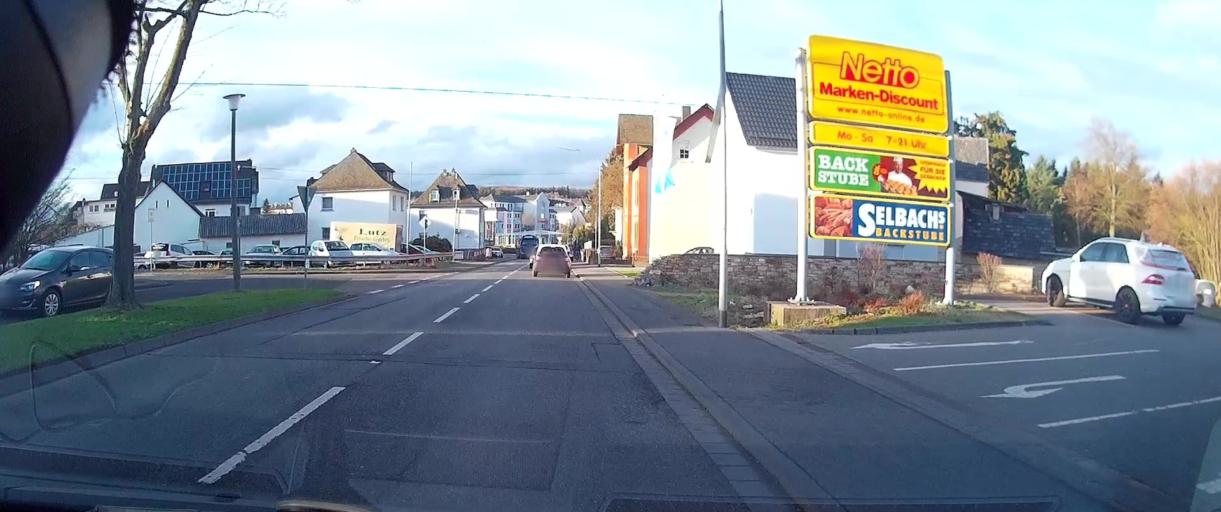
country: DE
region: Rheinland-Pfalz
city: Wirges
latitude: 50.4702
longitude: 7.7966
